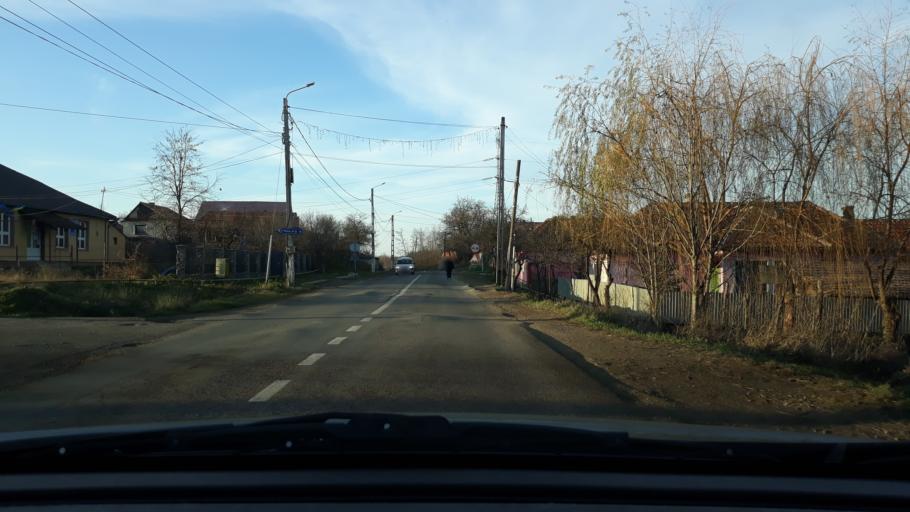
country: RO
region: Bihor
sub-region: Comuna Suplacu de Barcau
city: Suplacu de Barcau
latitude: 47.2626
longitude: 22.5171
